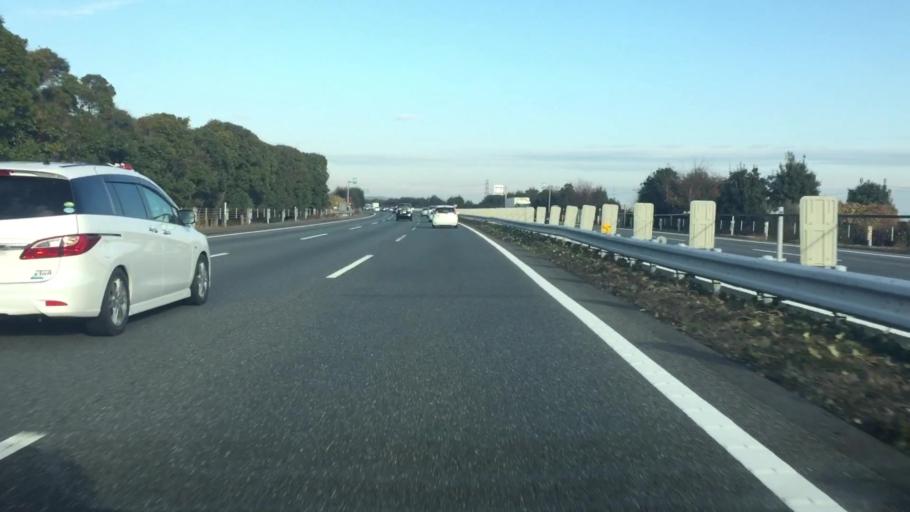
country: JP
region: Saitama
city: Honjo
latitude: 36.1904
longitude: 139.1896
